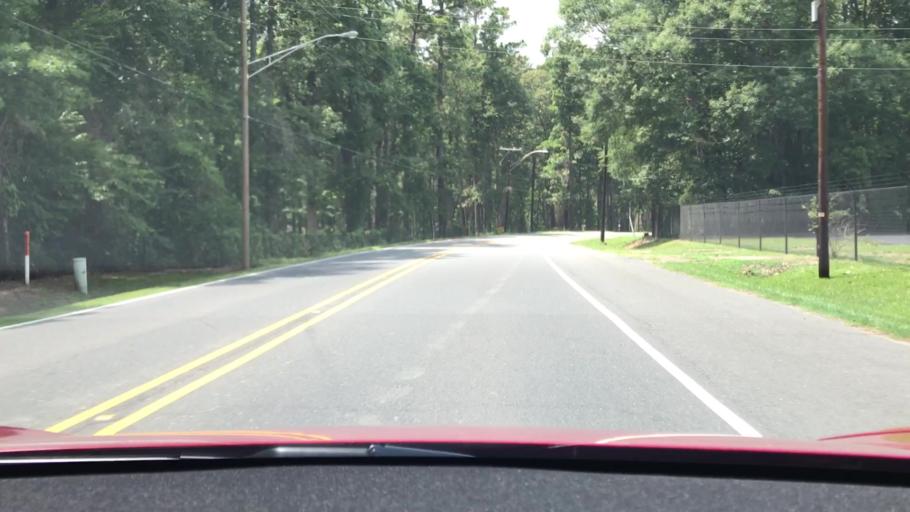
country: US
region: Louisiana
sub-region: Bossier Parish
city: Bossier City
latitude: 32.3911
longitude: -93.7234
